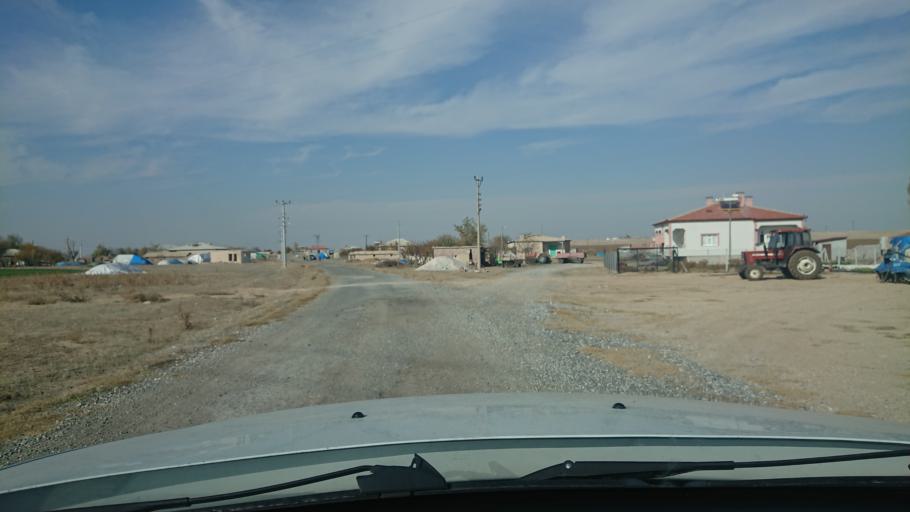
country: TR
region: Aksaray
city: Sultanhani
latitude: 38.2538
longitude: 33.4812
